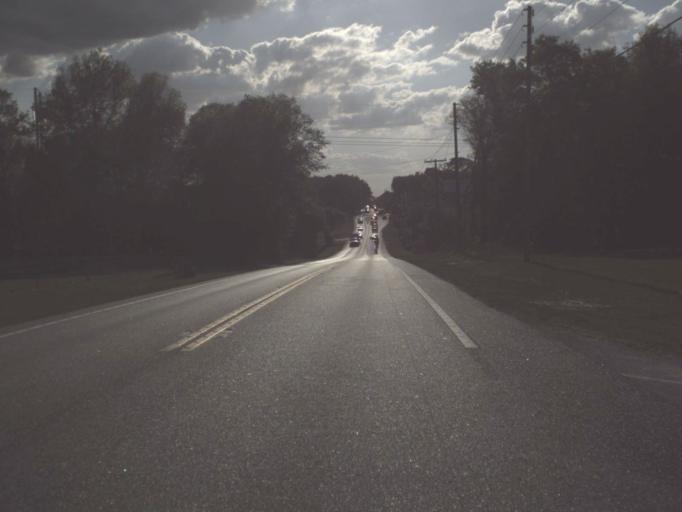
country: US
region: Florida
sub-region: Lake County
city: Mount Plymouth
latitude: 28.8080
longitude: -81.5468
